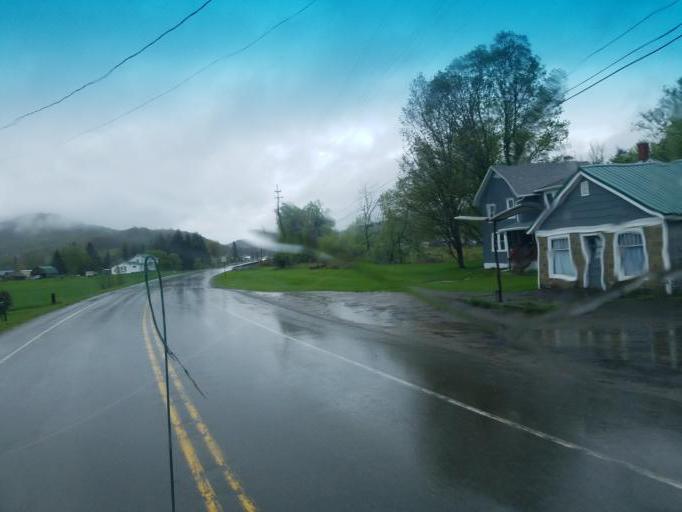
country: US
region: Pennsylvania
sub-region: Tioga County
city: Westfield
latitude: 41.9196
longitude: -77.6231
